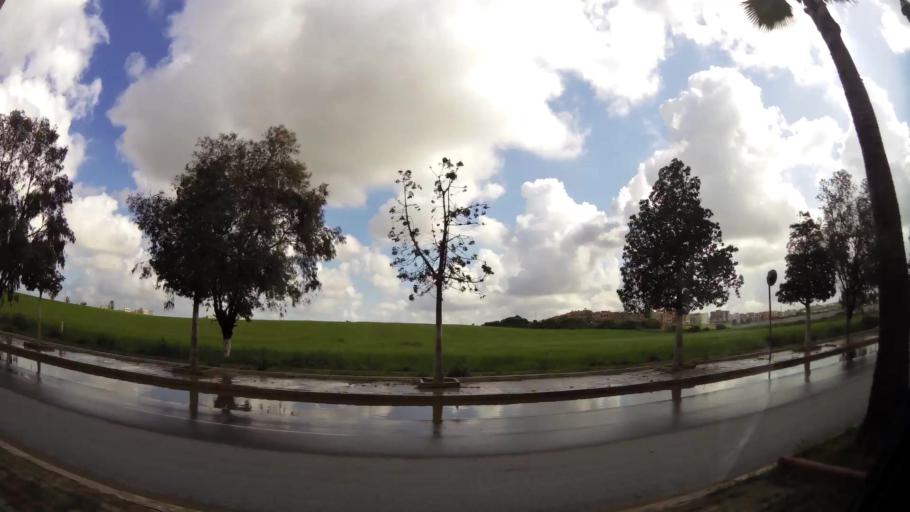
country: MA
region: Grand Casablanca
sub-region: Mediouna
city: Tit Mellil
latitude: 33.5598
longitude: -7.4902
